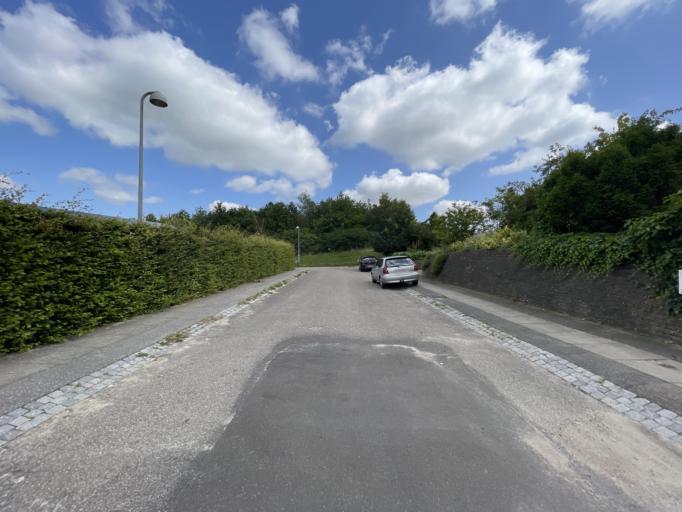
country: DK
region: Zealand
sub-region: Roskilde Kommune
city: Gundsomagle
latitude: 55.7406
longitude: 12.1551
